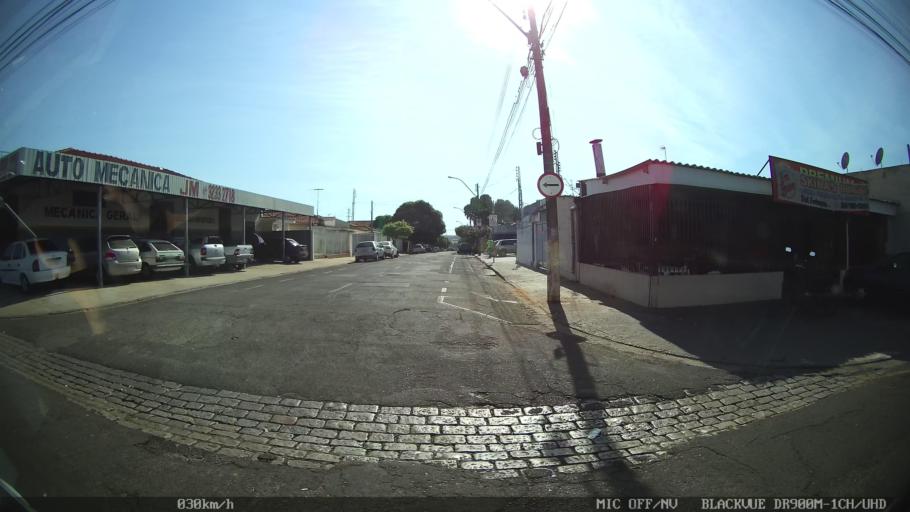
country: BR
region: Sao Paulo
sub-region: Sao Jose Do Rio Preto
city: Sao Jose do Rio Preto
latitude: -20.7976
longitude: -49.3865
